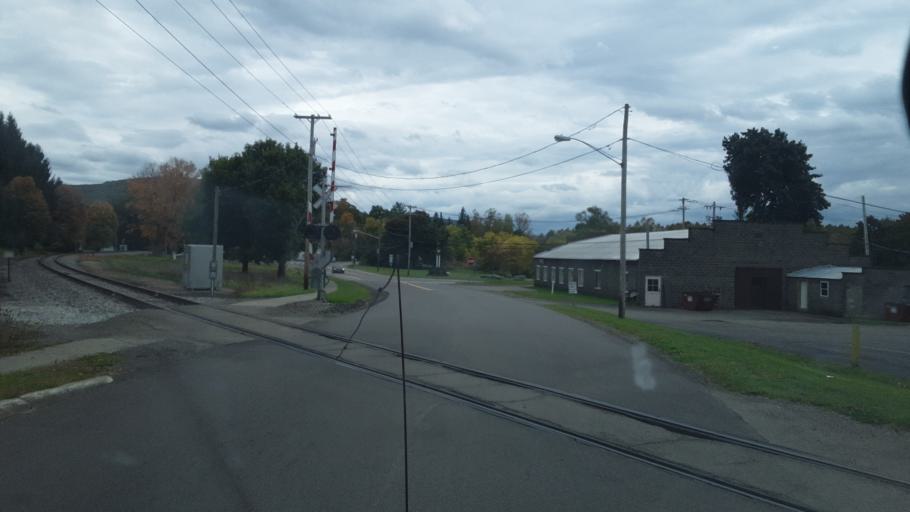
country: US
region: New York
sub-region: Allegany County
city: Belmont
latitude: 42.2259
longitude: -78.0311
